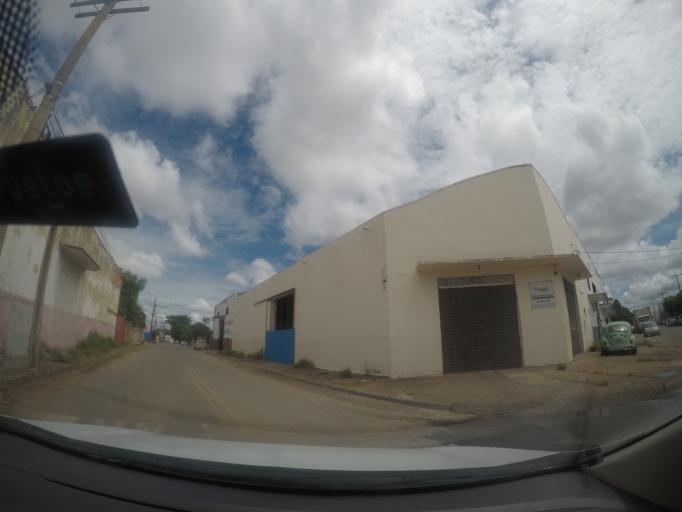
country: BR
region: Goias
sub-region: Goiania
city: Goiania
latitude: -16.6635
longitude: -49.3068
